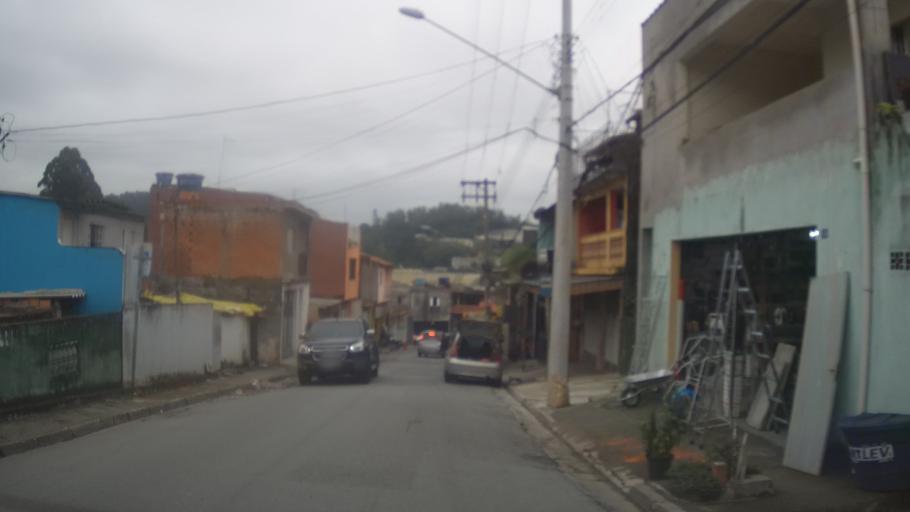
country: BR
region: Sao Paulo
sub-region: Guarulhos
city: Guarulhos
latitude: -23.4269
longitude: -46.5127
